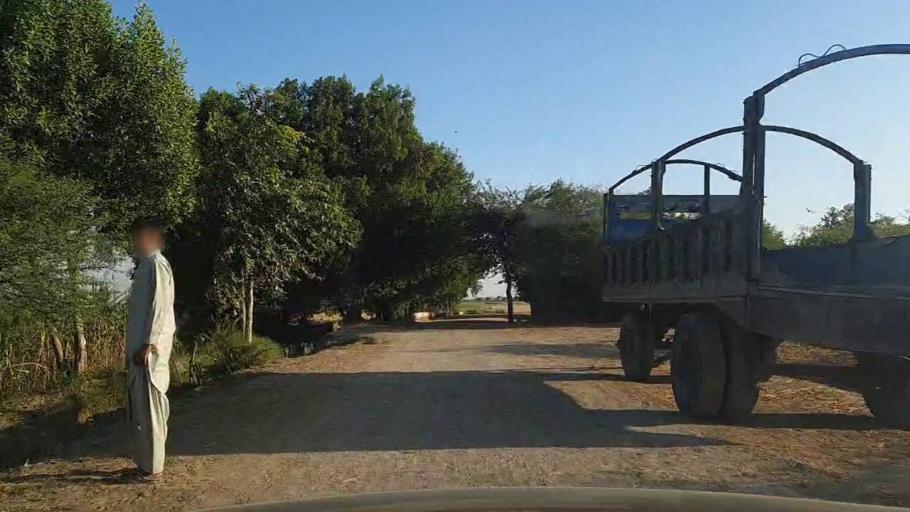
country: PK
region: Sindh
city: Mirpur Batoro
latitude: 24.7080
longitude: 68.3212
